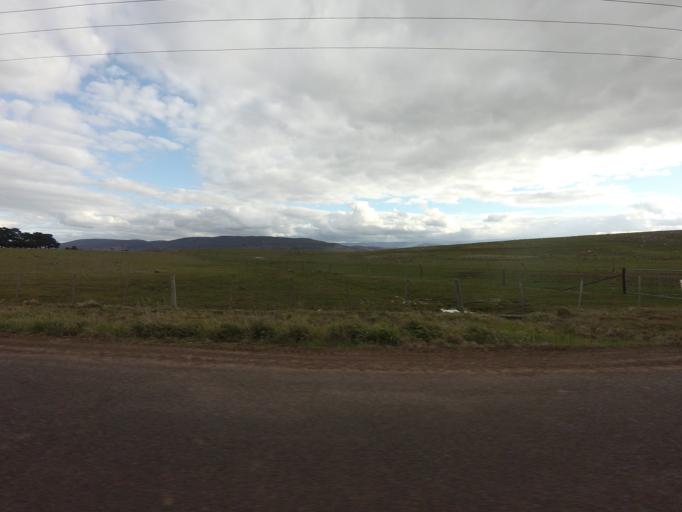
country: AU
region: Tasmania
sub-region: Northern Midlands
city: Evandale
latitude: -41.8980
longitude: 147.4360
